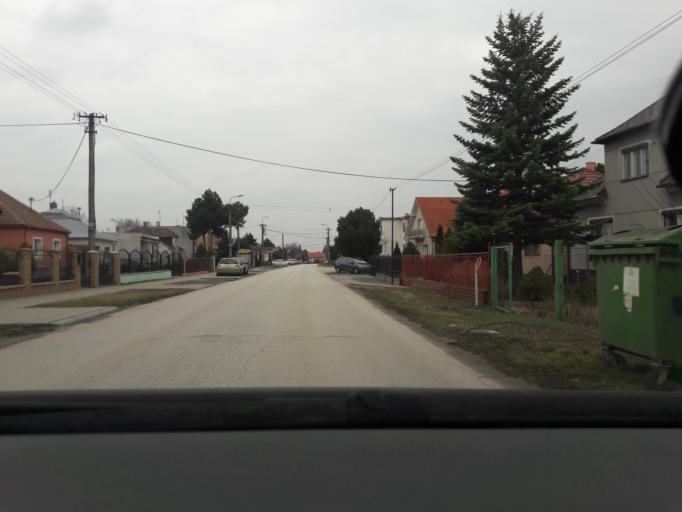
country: SK
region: Bratislavsky
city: Senec
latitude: 48.2996
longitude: 17.4513
